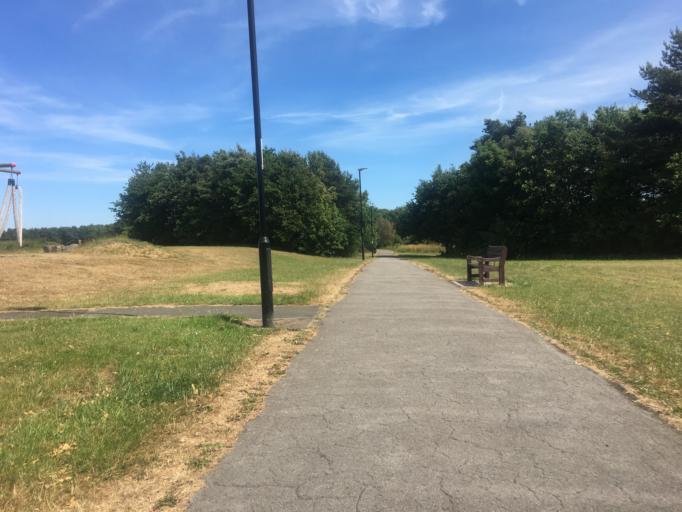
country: GB
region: England
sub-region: County Durham
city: Chester-le-Street
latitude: 54.8784
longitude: -1.5490
